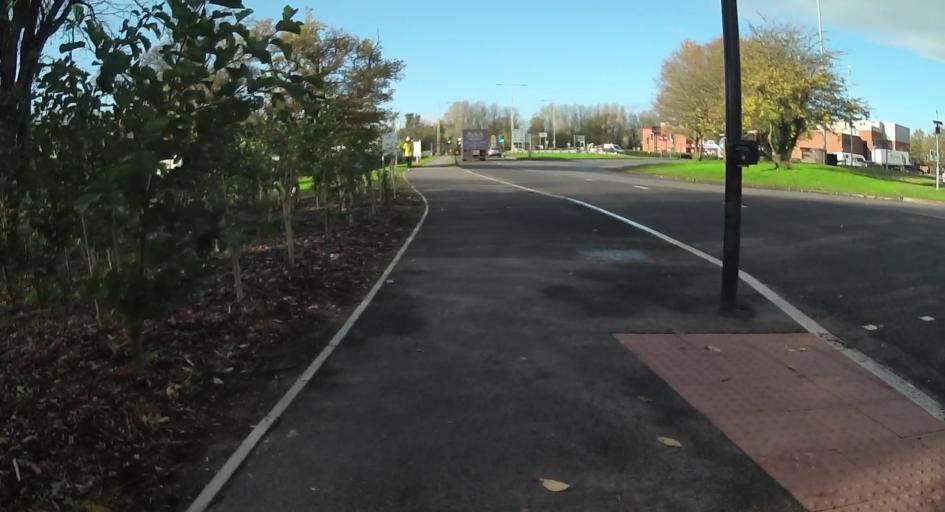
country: GB
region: England
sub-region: Wokingham
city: Winnersh
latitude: 51.4356
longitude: -0.8972
